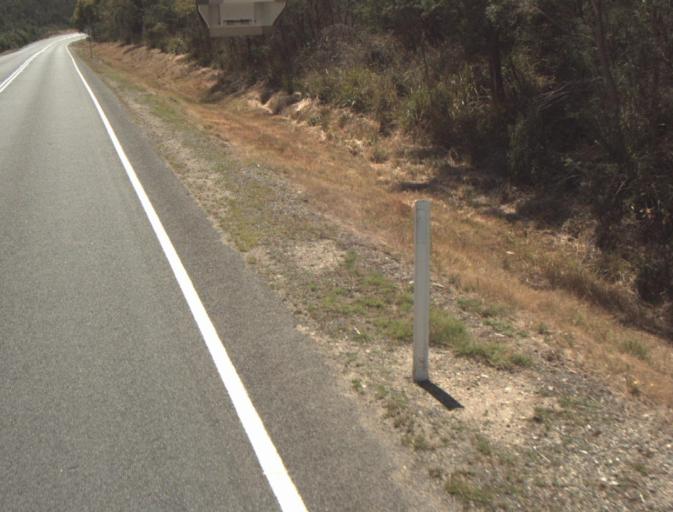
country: AU
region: Tasmania
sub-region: Launceston
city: Mayfield
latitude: -41.3628
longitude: 147.1446
